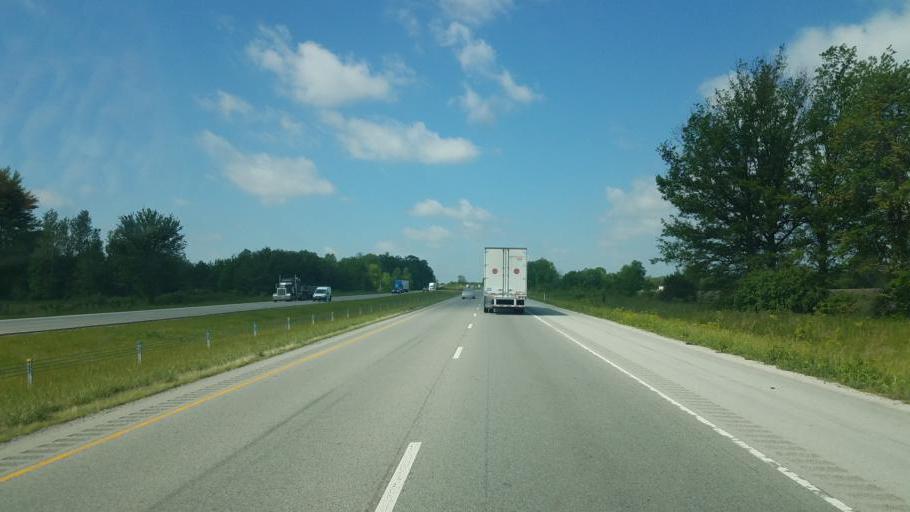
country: US
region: Indiana
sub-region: Clay County
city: Brazil
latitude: 39.4762
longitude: -87.0187
